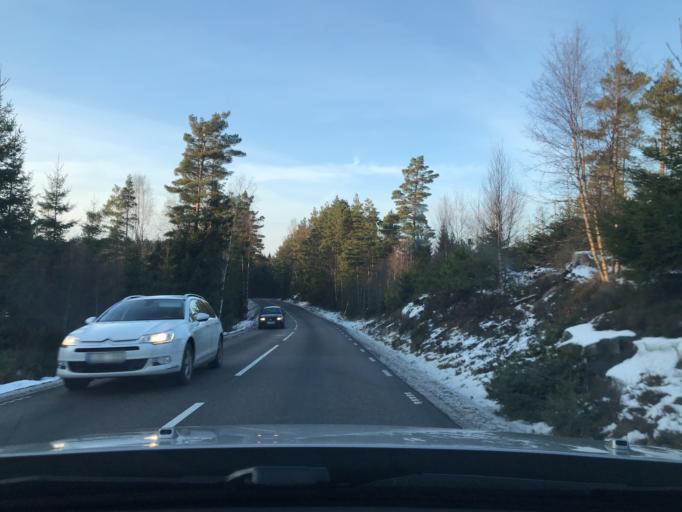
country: SE
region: Vaestra Goetaland
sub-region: Lerums Kommun
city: Stenkullen
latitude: 57.7137
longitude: 12.3475
